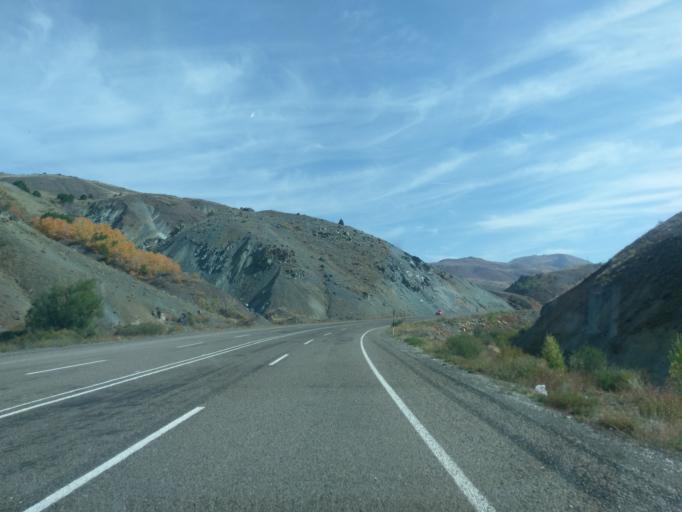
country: TR
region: Sivas
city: Imranli
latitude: 39.8559
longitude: 38.3078
